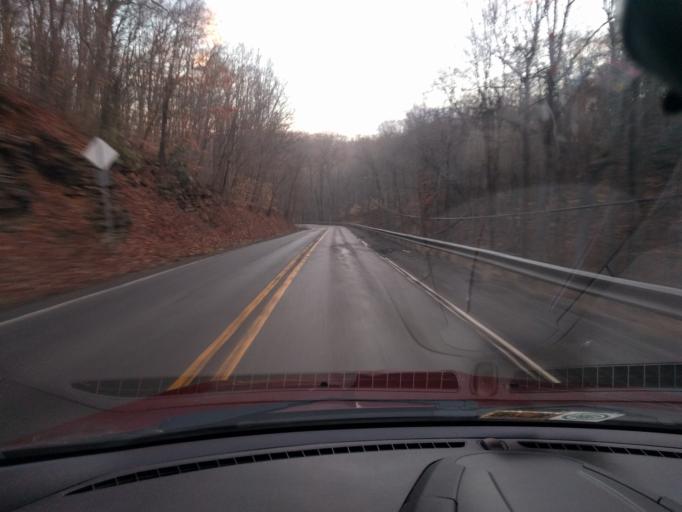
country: US
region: West Virginia
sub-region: Greenbrier County
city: Rainelle
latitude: 38.0249
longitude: -80.9156
